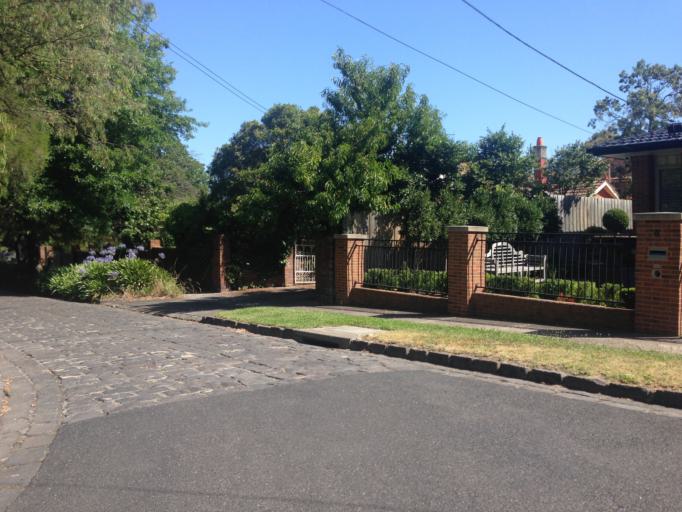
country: AU
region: Victoria
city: Alphington
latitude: -37.7813
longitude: 145.0404
